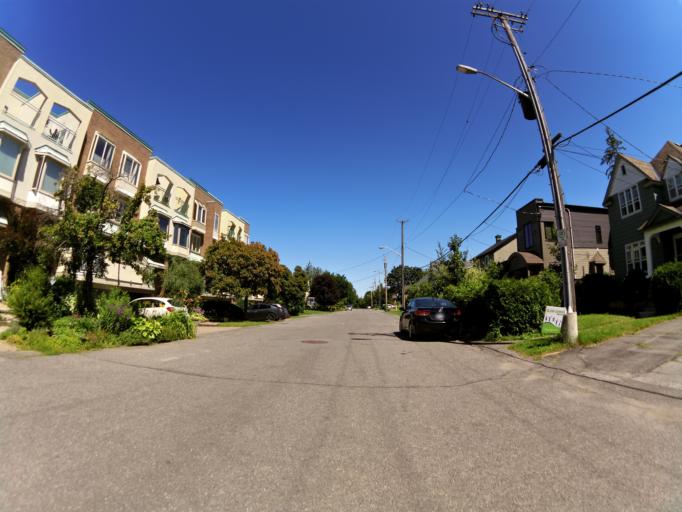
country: CA
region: Ontario
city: Ottawa
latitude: 45.4262
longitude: -75.6659
